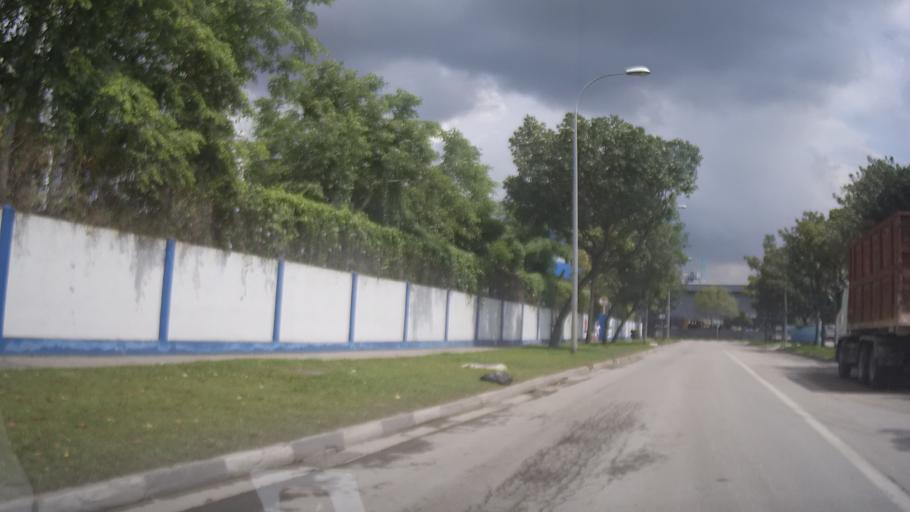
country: MY
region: Johor
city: Johor Bahru
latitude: 1.4328
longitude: 103.7494
